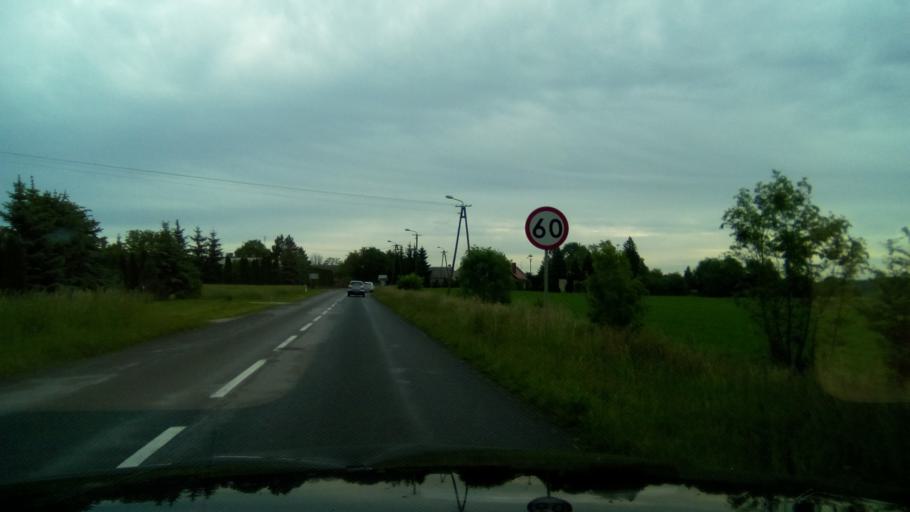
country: PL
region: Kujawsko-Pomorskie
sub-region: Powiat sepolenski
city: Wiecbork
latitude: 53.3915
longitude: 17.5188
